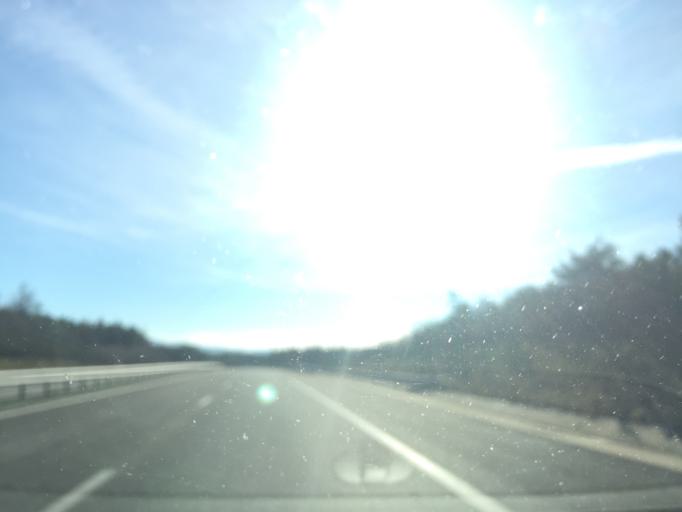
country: FR
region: Auvergne
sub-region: Departement du Puy-de-Dome
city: Gelles
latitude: 45.7157
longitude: 2.6938
